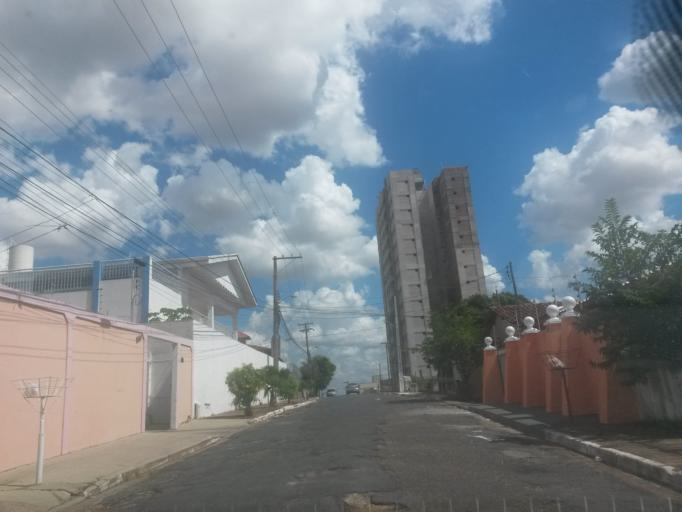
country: BR
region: Mato Grosso
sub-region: Cuiaba
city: Cuiaba
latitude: -15.6024
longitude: -56.0767
